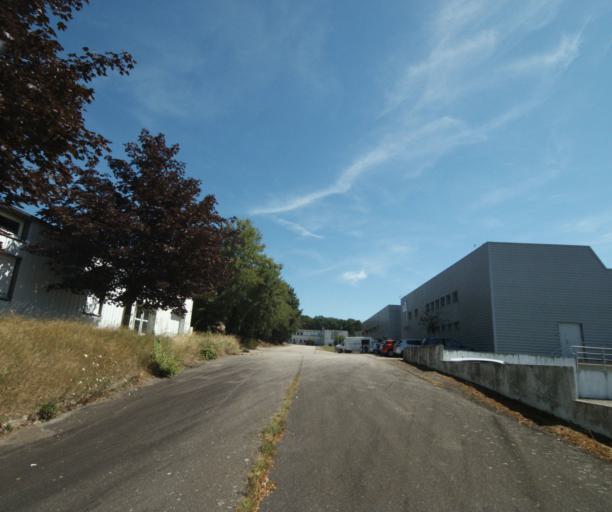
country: FR
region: Lorraine
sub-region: Departement des Vosges
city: Golbey
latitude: 48.2011
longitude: 6.4513
